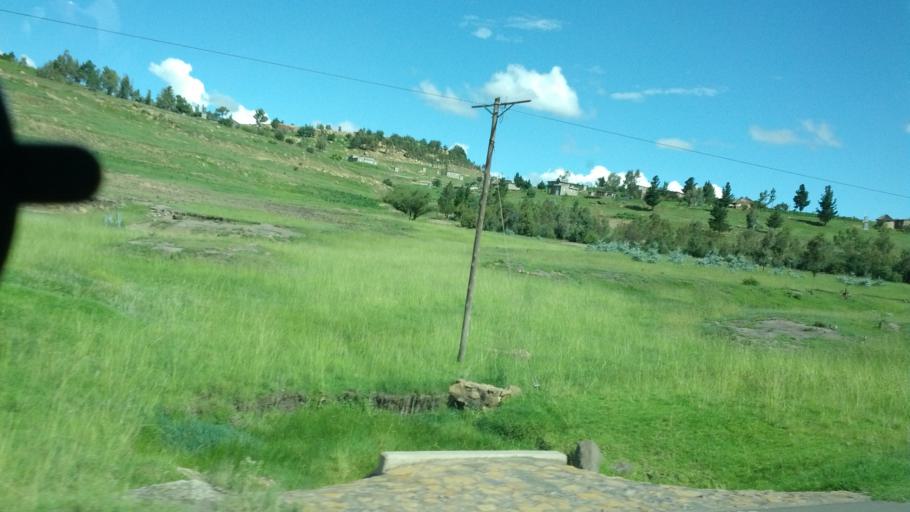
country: LS
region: Maseru
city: Maseru
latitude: -29.5346
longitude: 27.5101
